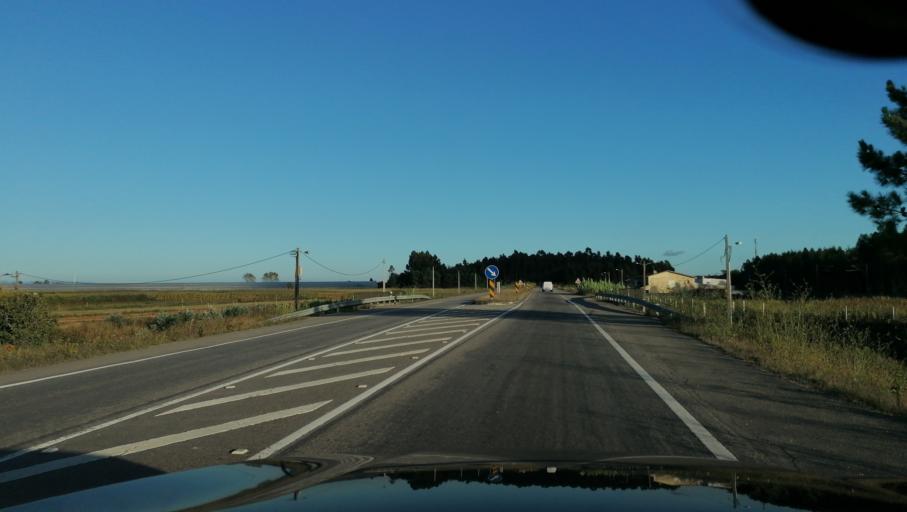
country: PT
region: Aveiro
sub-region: Aveiro
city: Oliveirinha
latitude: 40.6010
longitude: -8.6177
